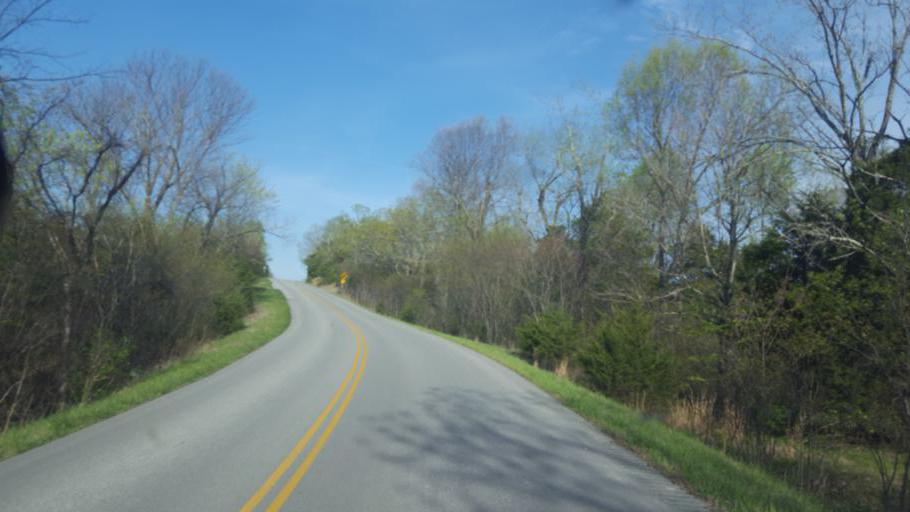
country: US
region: Kentucky
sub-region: Hart County
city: Munfordville
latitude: 37.3148
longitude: -86.0752
